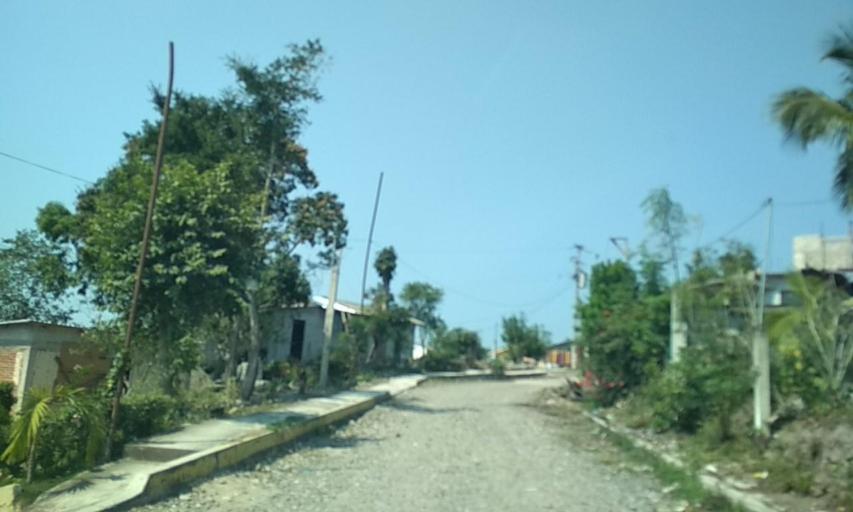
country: MX
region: Veracruz
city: Gutierrez Zamora
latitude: 20.4235
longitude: -97.1900
